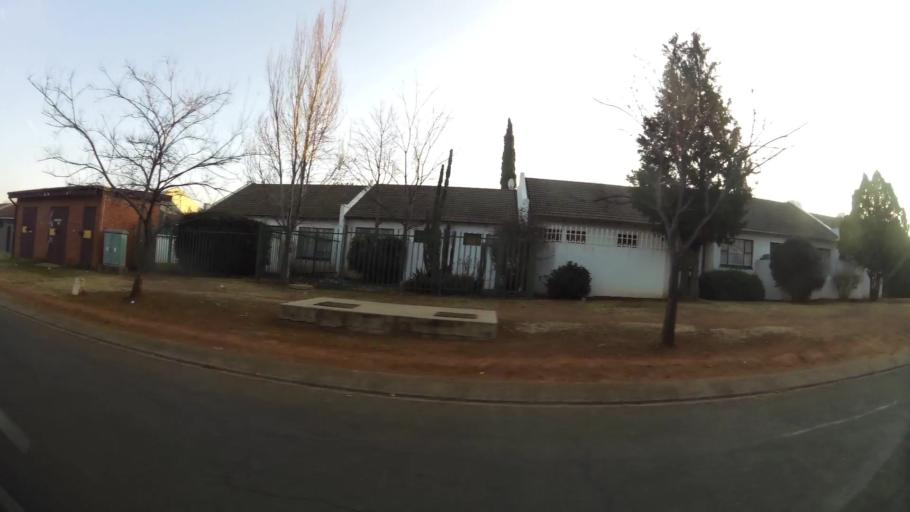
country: ZA
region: Orange Free State
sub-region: Mangaung Metropolitan Municipality
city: Bloemfontein
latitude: -29.1017
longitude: 26.1609
